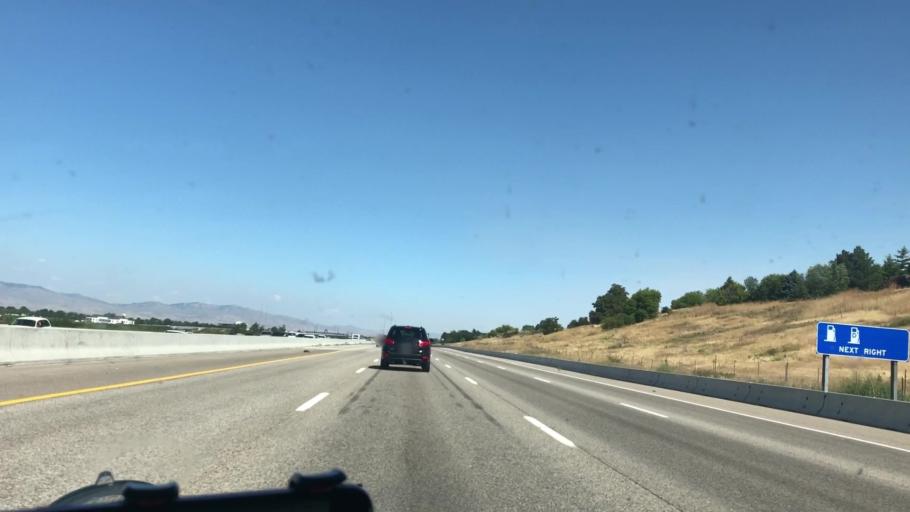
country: US
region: Idaho
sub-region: Ada County
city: Meridian
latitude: 43.5941
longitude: -116.4487
